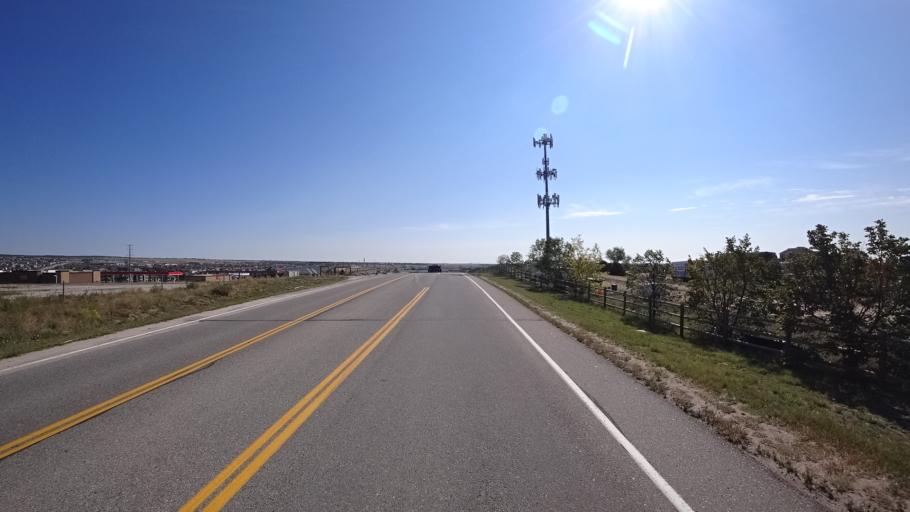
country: US
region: Colorado
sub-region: El Paso County
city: Black Forest
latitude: 38.9389
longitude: -104.7029
